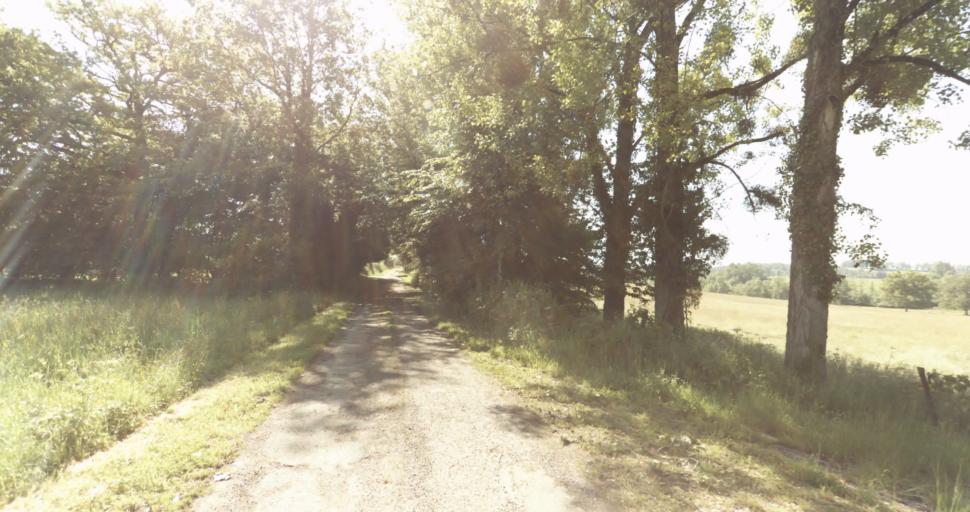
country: FR
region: Limousin
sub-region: Departement de la Haute-Vienne
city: Le Vigen
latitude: 45.7177
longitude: 1.2776
